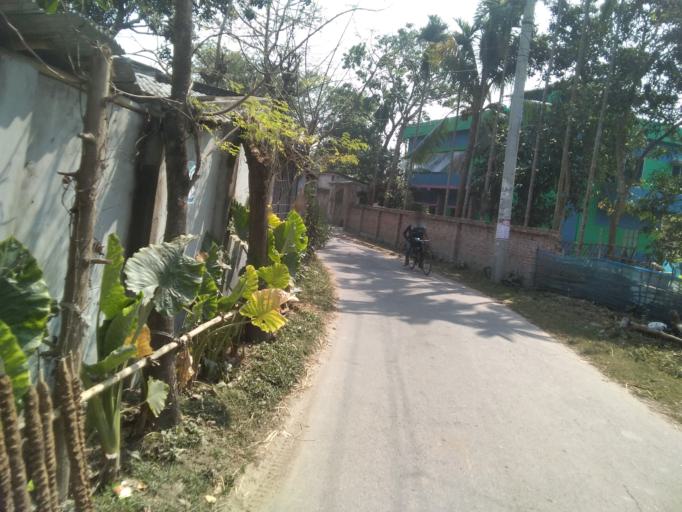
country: IN
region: West Bengal
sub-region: North 24 Parganas
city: Taki
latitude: 22.5913
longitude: 88.9955
